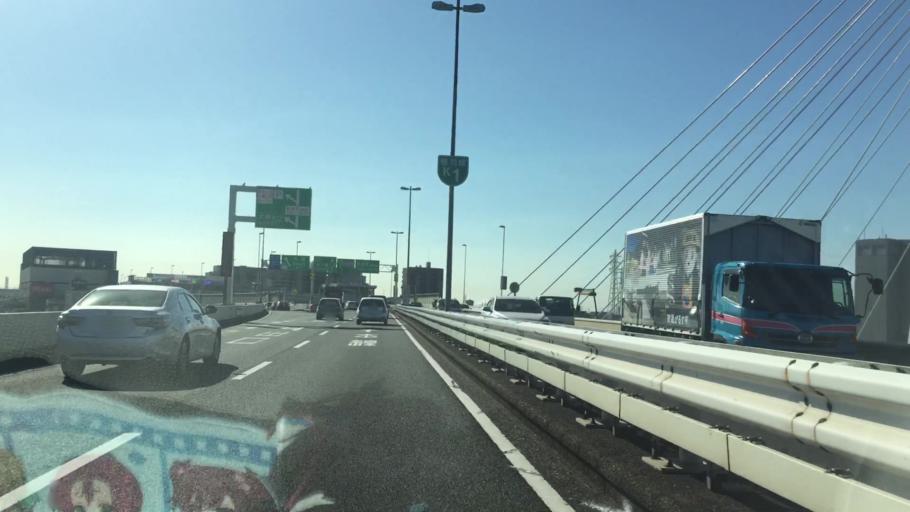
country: JP
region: Kanagawa
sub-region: Kawasaki-shi
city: Kawasaki
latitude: 35.5419
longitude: 139.7420
